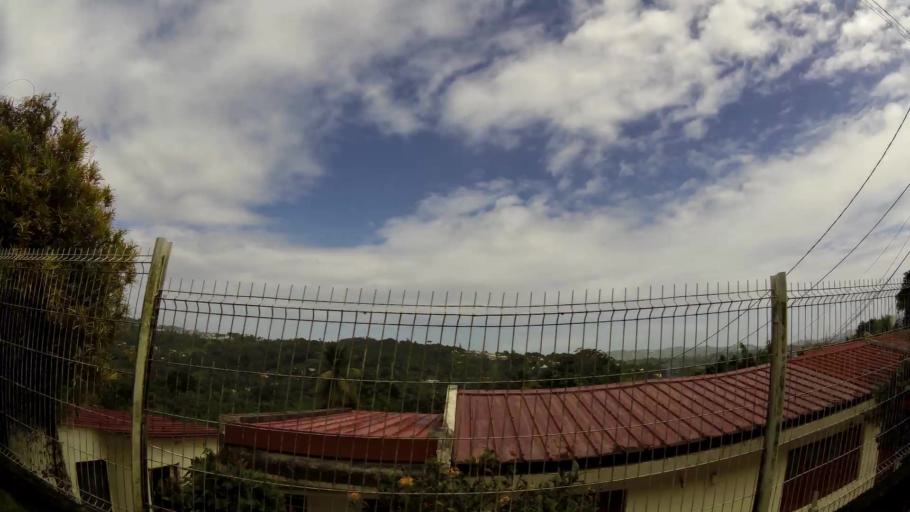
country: MQ
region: Martinique
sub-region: Martinique
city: Saint-Joseph
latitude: 14.6539
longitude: -61.0373
